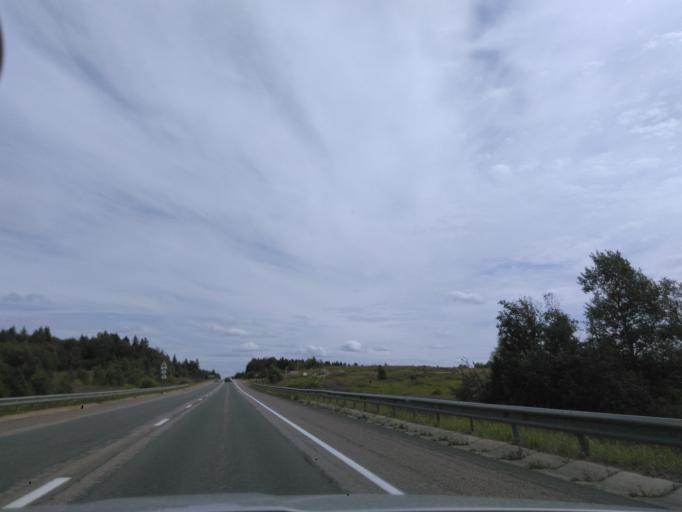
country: RU
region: Moskovskaya
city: Solnechnogorsk
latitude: 56.1431
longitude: 36.9557
